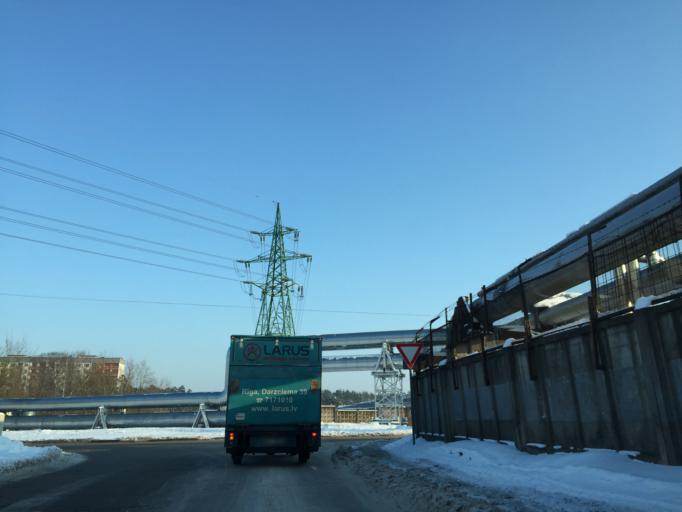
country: LV
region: Stopini
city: Ulbroka
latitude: 56.9306
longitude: 24.2105
